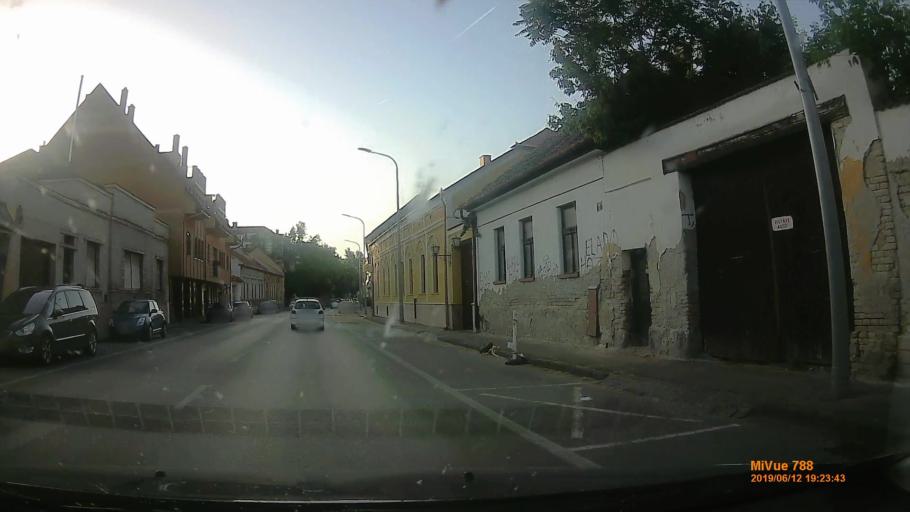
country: HU
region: Bacs-Kiskun
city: Kecskemet
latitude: 46.9122
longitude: 19.6906
